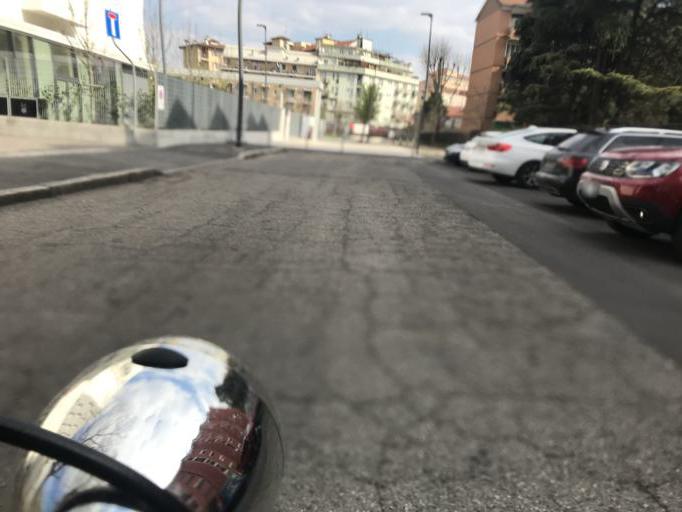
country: IT
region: Lombardy
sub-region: Citta metropolitana di Milano
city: Novate Milanese
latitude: 45.5033
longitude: 9.1446
